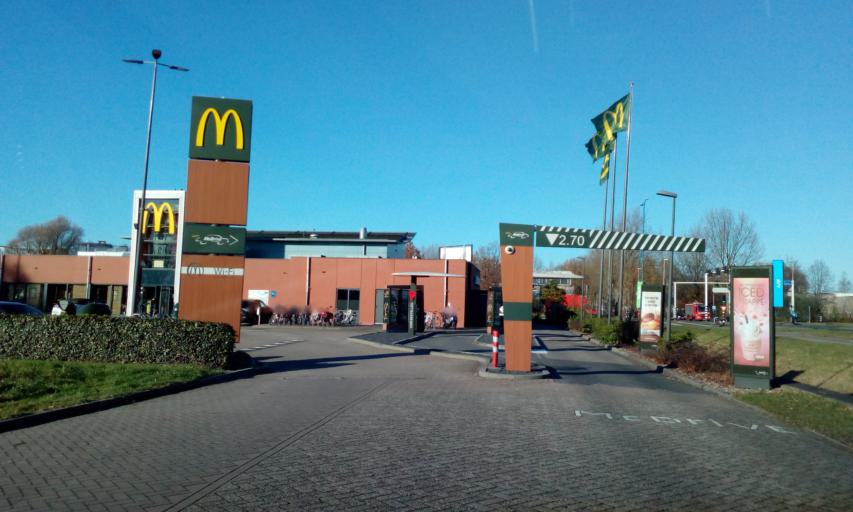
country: NL
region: South Holland
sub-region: Gemeente Rijnwoude
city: Benthuizen
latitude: 52.0551
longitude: 4.5238
